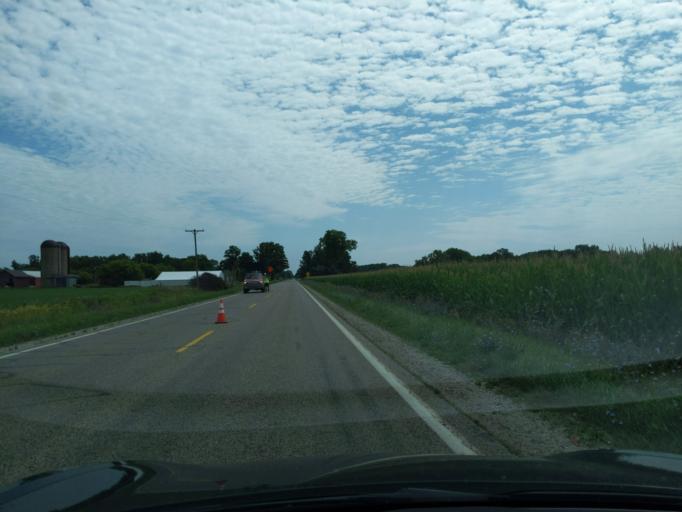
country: US
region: Michigan
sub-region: Gratiot County
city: Breckenridge
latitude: 43.2919
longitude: -84.4331
